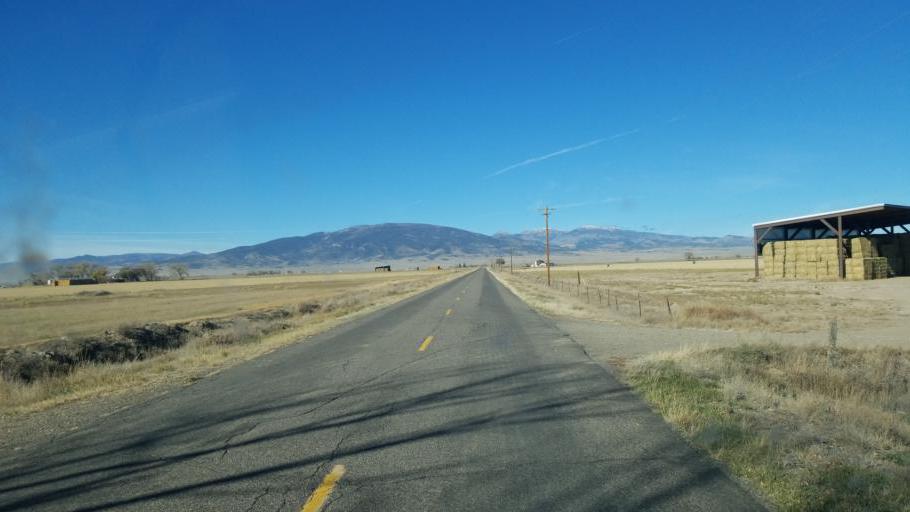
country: US
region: Colorado
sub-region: Rio Grande County
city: Monte Vista
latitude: 37.4591
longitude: -106.0849
